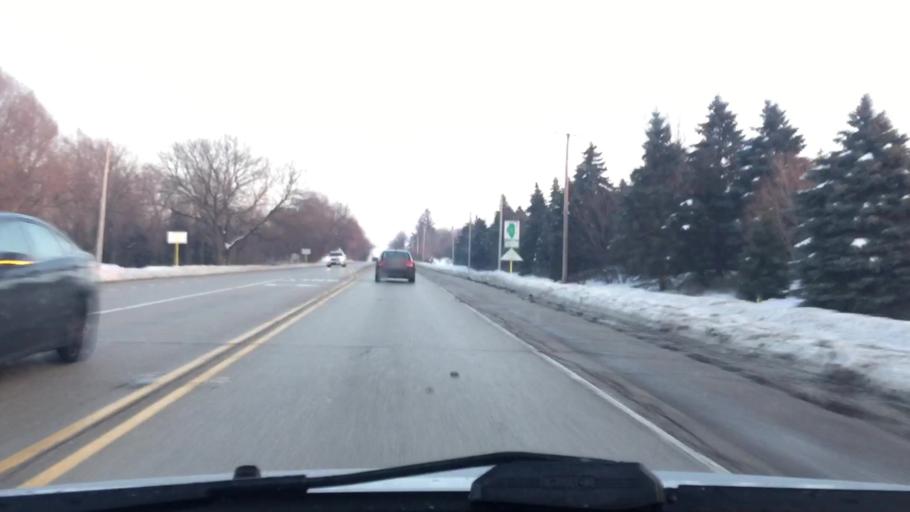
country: US
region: Illinois
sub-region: Kane County
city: Village of Campton Hills
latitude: 41.9293
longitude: -88.3772
